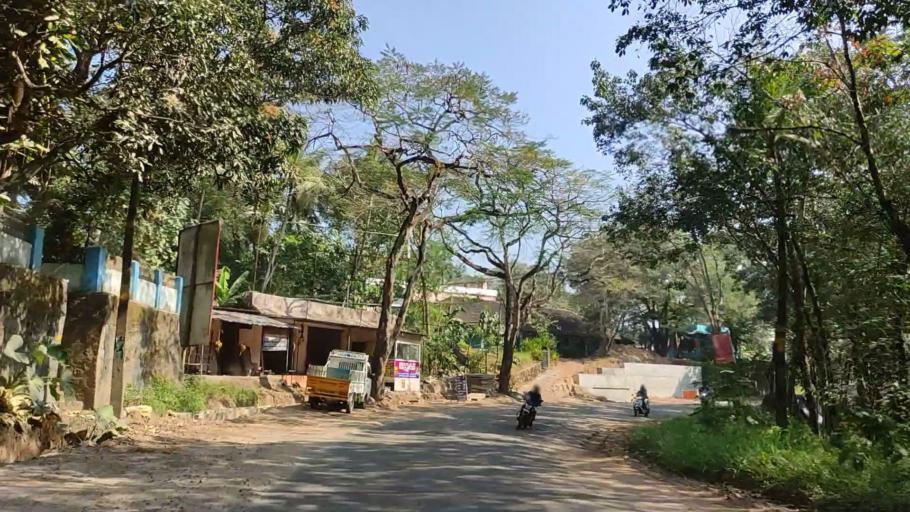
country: IN
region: Kerala
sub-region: Kollam
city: Punalur
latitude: 8.9056
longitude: 76.8746
